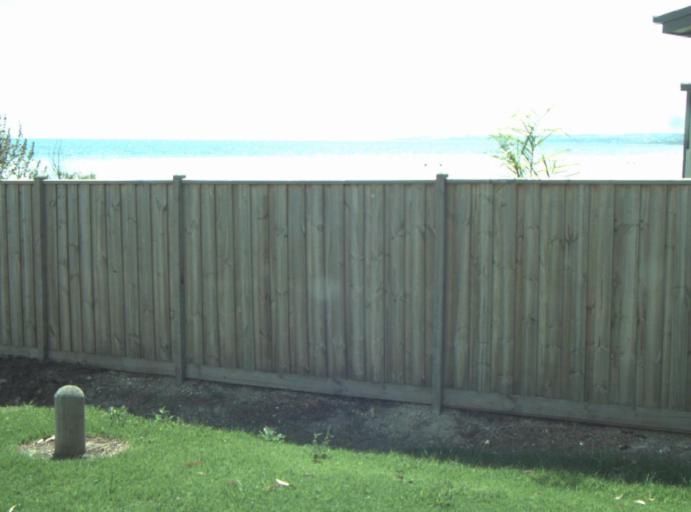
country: AU
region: Victoria
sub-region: Greater Geelong
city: Leopold
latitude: -38.1583
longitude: 144.4566
